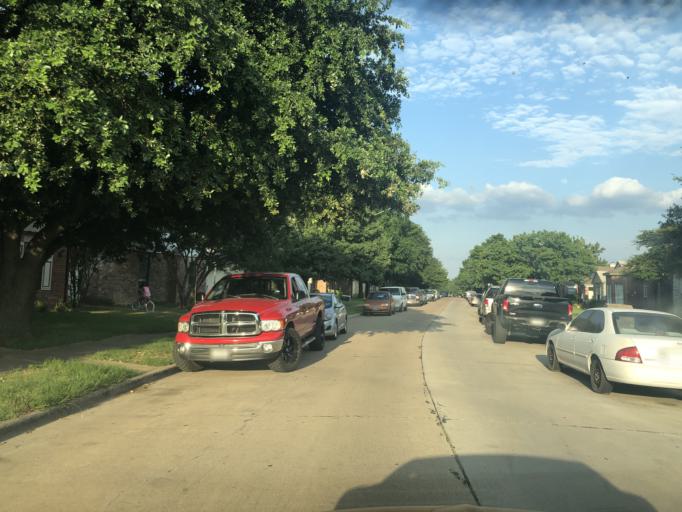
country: US
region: Texas
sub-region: Dallas County
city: Irving
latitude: 32.7909
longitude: -96.9471
